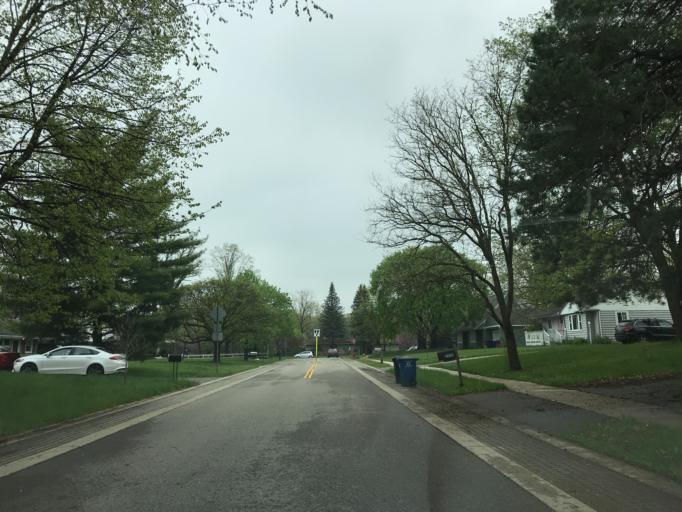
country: US
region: Michigan
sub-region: Washtenaw County
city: Ann Arbor
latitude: 42.2459
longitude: -83.7081
